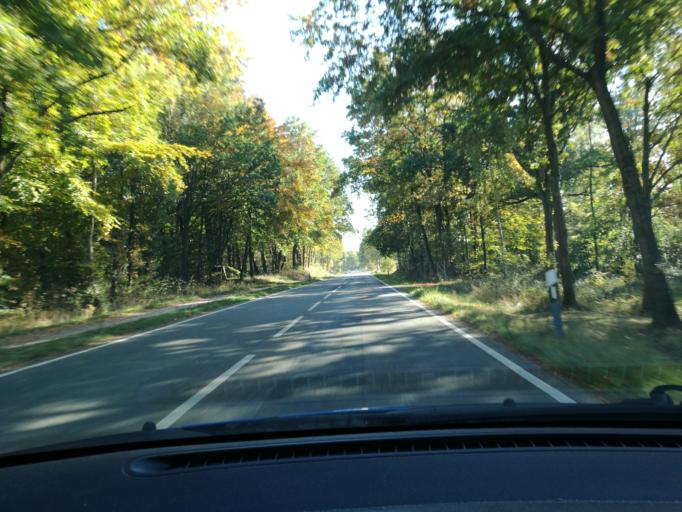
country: DE
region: Lower Saxony
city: Vastorf
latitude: 53.2063
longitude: 10.5327
